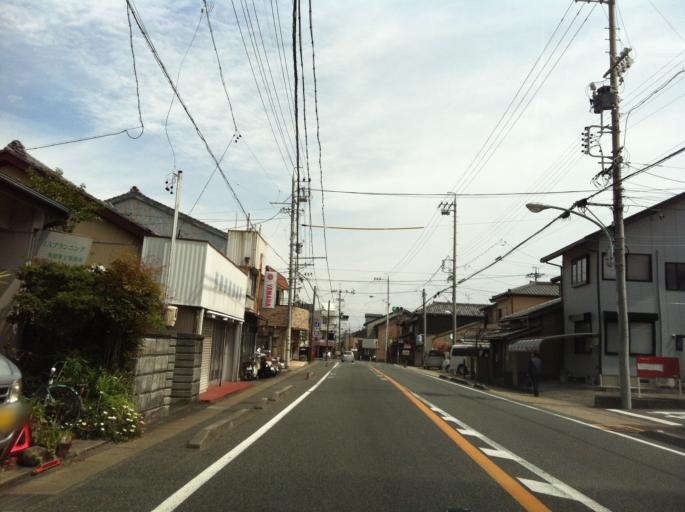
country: JP
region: Shizuoka
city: Fuji
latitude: 35.1176
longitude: 138.6008
